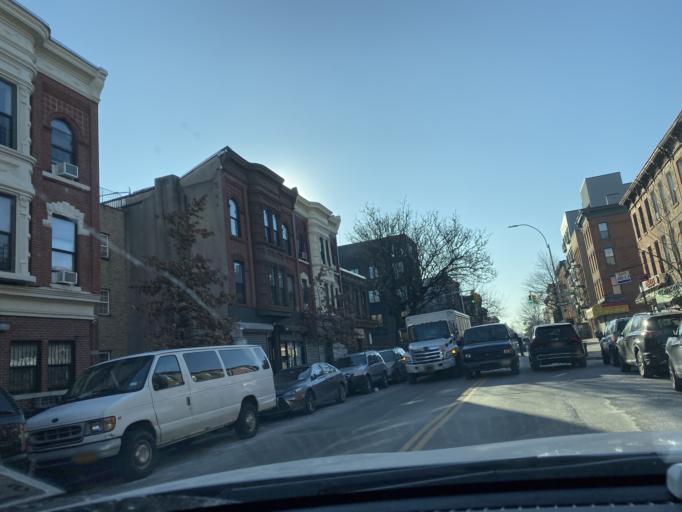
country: US
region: New York
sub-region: Kings County
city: Brooklyn
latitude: 40.6861
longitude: -73.9297
